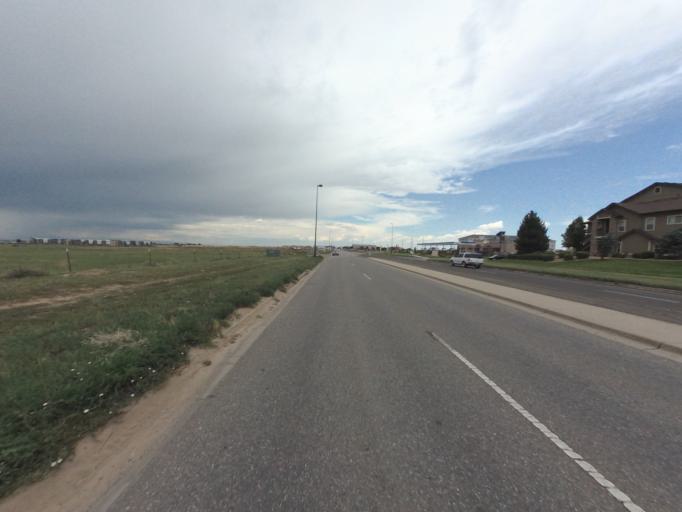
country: US
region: Colorado
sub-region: Adams County
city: Aurora
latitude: 39.8034
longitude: -104.7722
